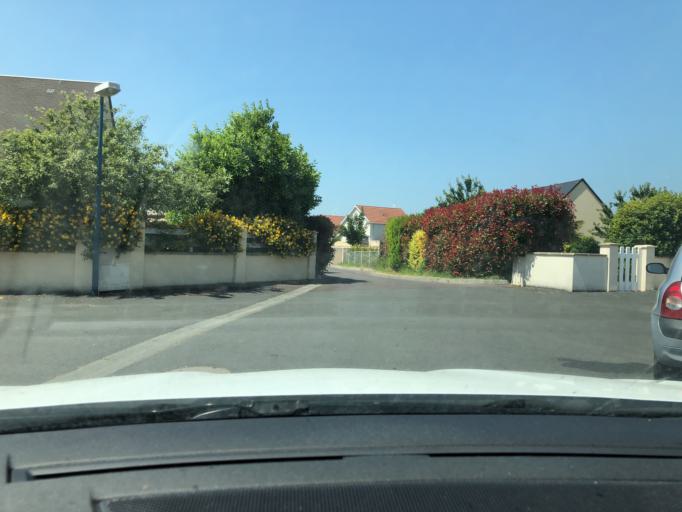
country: FR
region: Lower Normandy
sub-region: Departement du Calvados
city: Lion-sur-Mer
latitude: 49.3002
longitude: -0.3281
